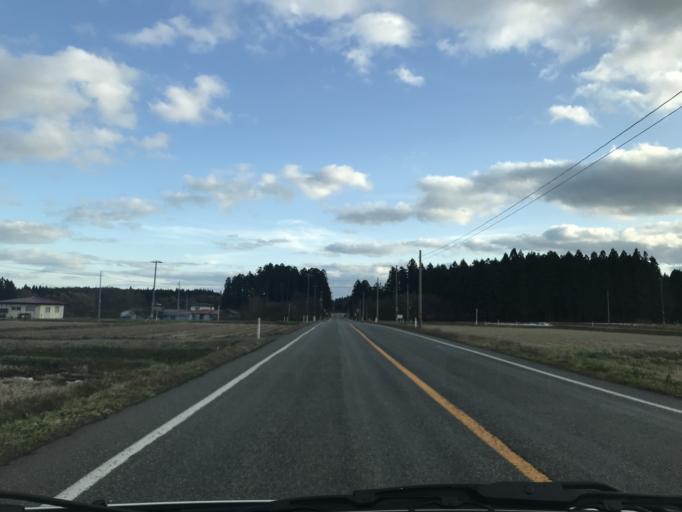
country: JP
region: Iwate
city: Mizusawa
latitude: 39.1649
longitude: 141.0488
